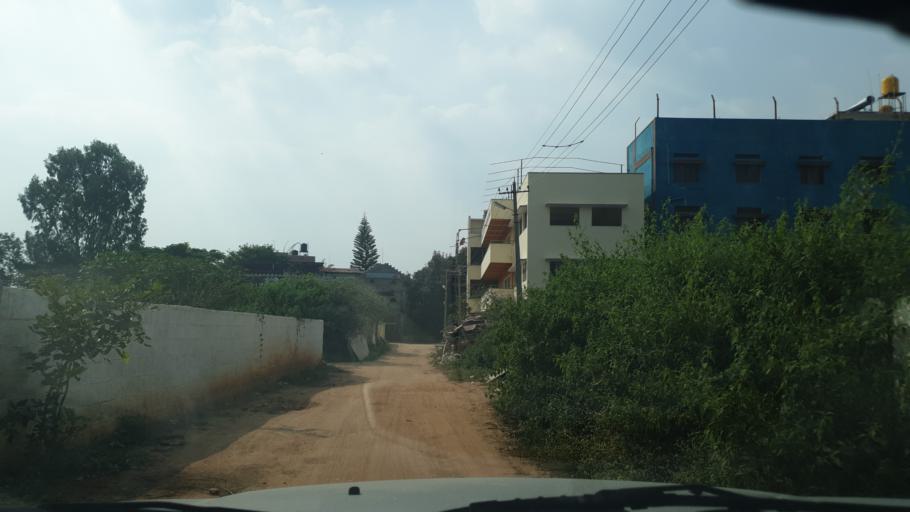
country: IN
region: Karnataka
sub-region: Bangalore Urban
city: Yelahanka
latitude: 13.0704
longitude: 77.6608
